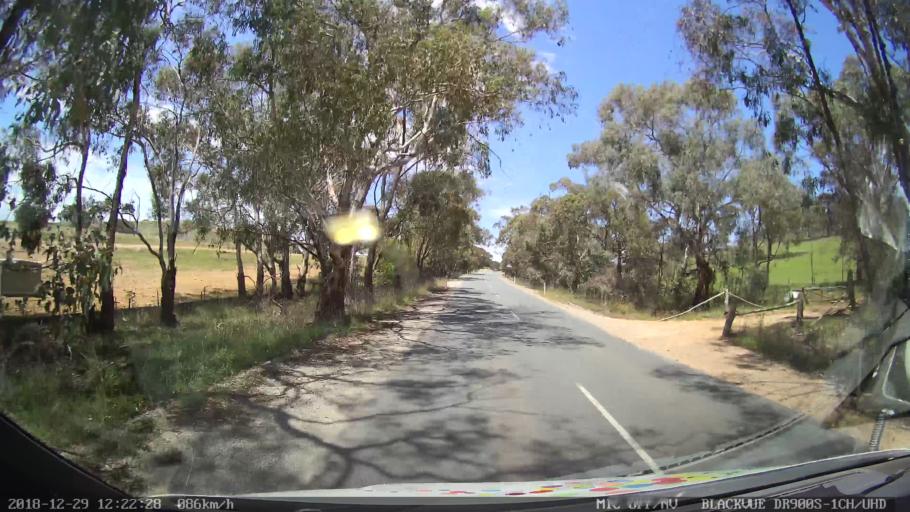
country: AU
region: New South Wales
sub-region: Queanbeyan
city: Queanbeyan
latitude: -35.4251
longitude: 149.2204
